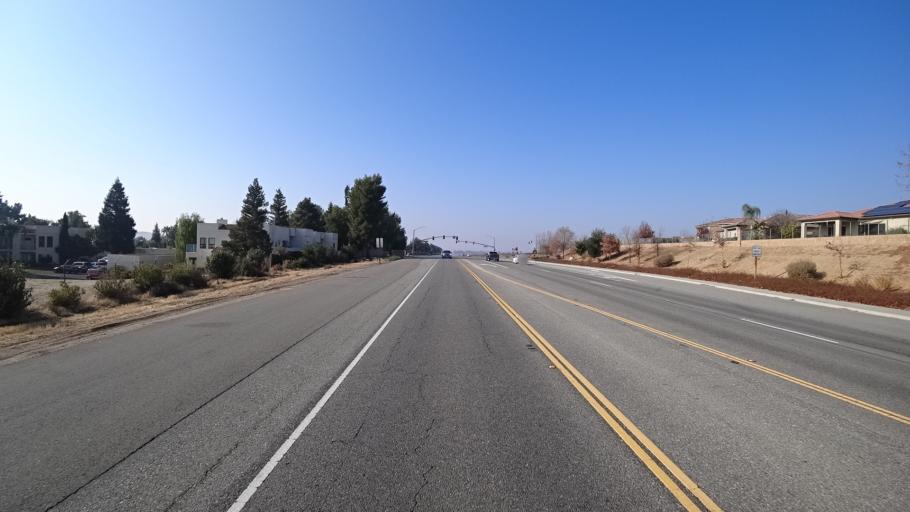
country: US
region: California
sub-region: Kern County
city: Lamont
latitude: 35.4130
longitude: -118.8427
